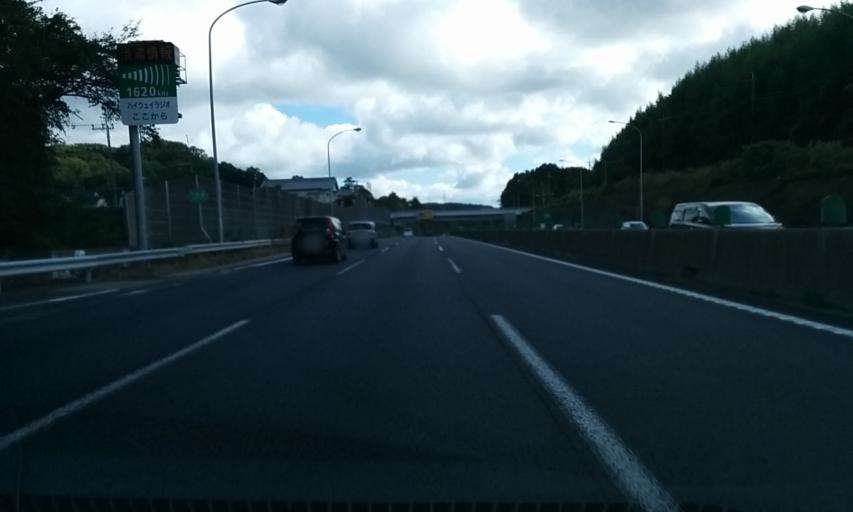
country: JP
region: Hyogo
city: Sandacho
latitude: 34.8353
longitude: 135.2663
